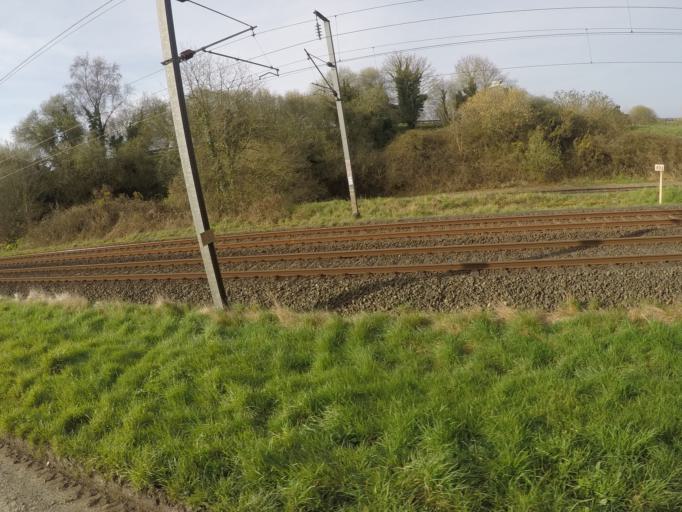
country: FR
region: Brittany
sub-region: Departement des Cotes-d'Armor
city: Plelo
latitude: 48.5308
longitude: -2.9637
